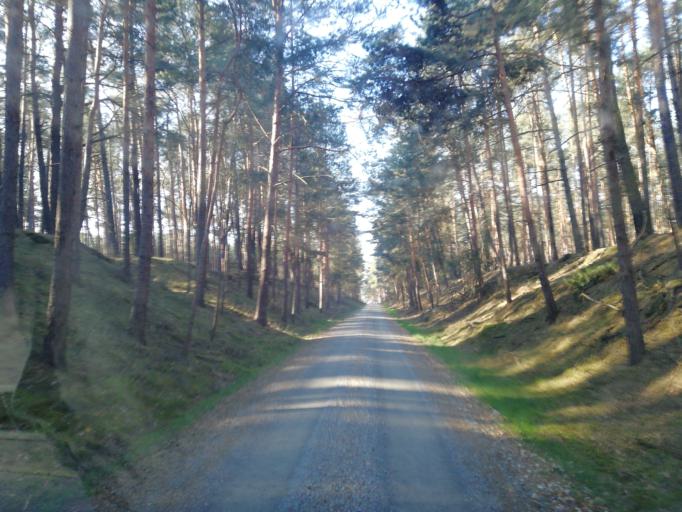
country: DE
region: Brandenburg
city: Drahnsdorf
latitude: 51.8914
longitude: 13.5268
